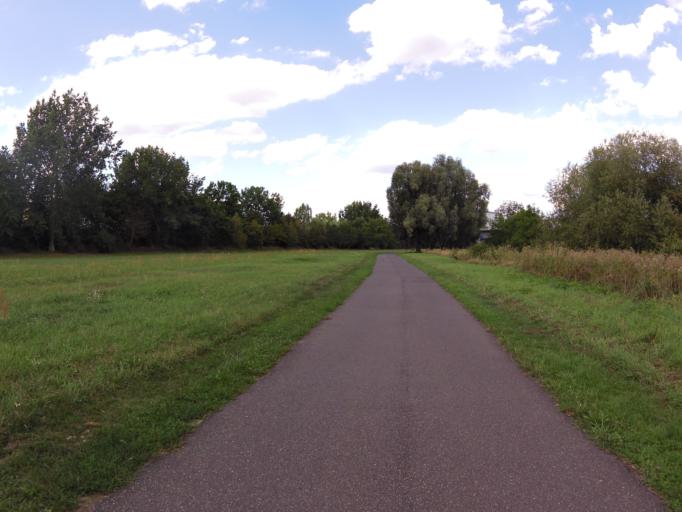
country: DE
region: Bavaria
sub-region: Regierungsbezirk Unterfranken
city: Schweinfurt
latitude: 50.0322
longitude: 10.2200
